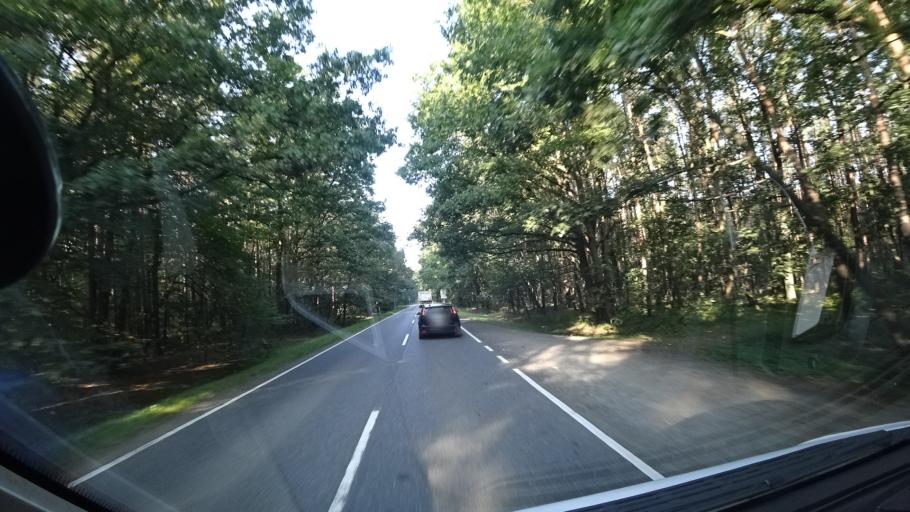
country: PL
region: Silesian Voivodeship
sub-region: Powiat raciborski
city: Rudy
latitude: 50.2686
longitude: 18.4314
